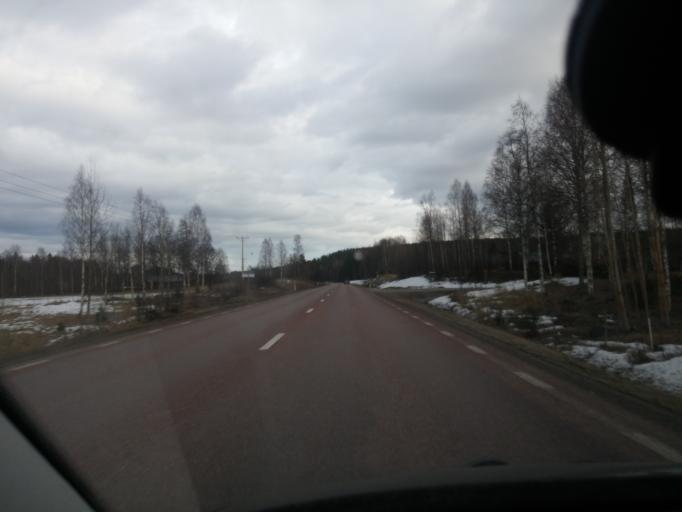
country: SE
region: Gaevleborg
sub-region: Ljusdals Kommun
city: Ljusdal
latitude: 61.8114
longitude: 16.0908
